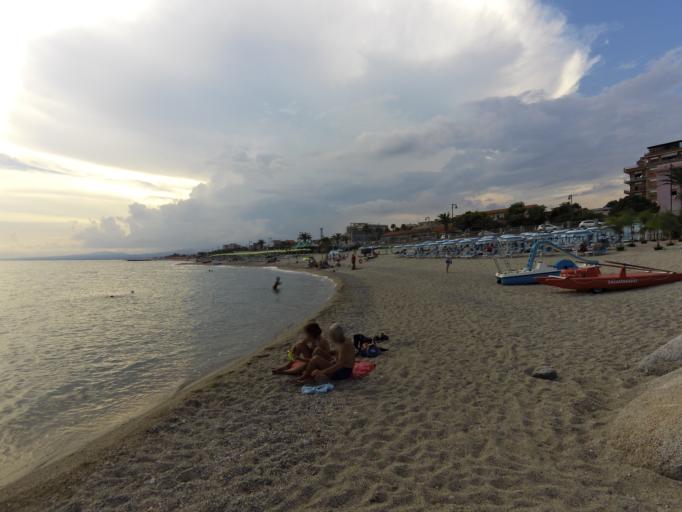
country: IT
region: Calabria
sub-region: Provincia di Reggio Calabria
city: Roccella Ionica
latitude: 38.3196
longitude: 16.4032
